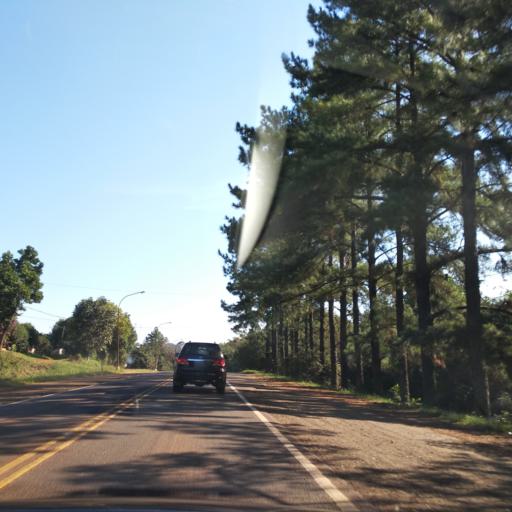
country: AR
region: Misiones
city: Gobernador Roca
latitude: -27.1808
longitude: -55.4586
